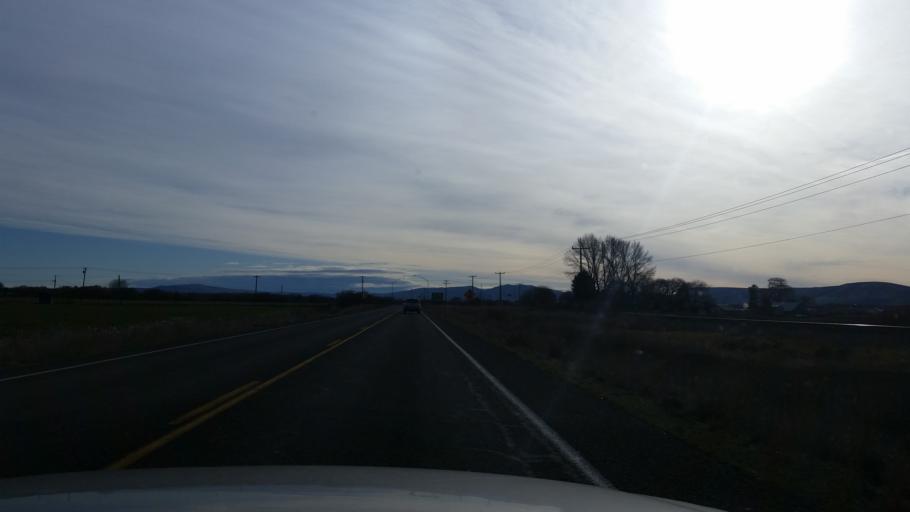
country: US
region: Washington
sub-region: Kittitas County
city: Ellensburg
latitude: 47.0240
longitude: -120.5955
